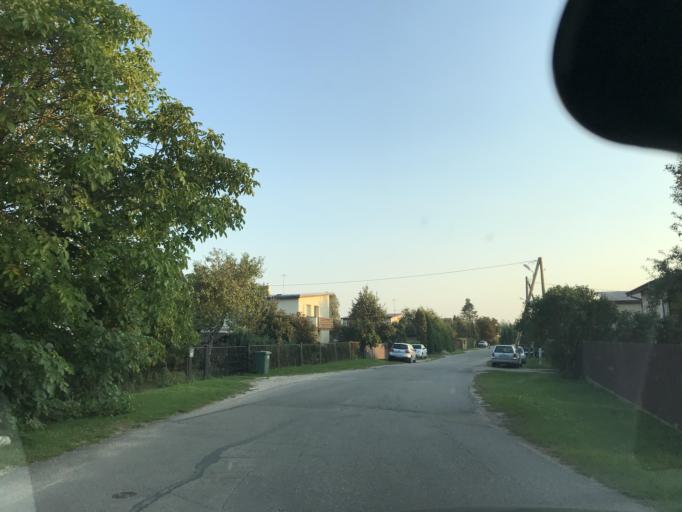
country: LV
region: Ikskile
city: Ikskile
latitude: 56.8288
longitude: 24.5054
